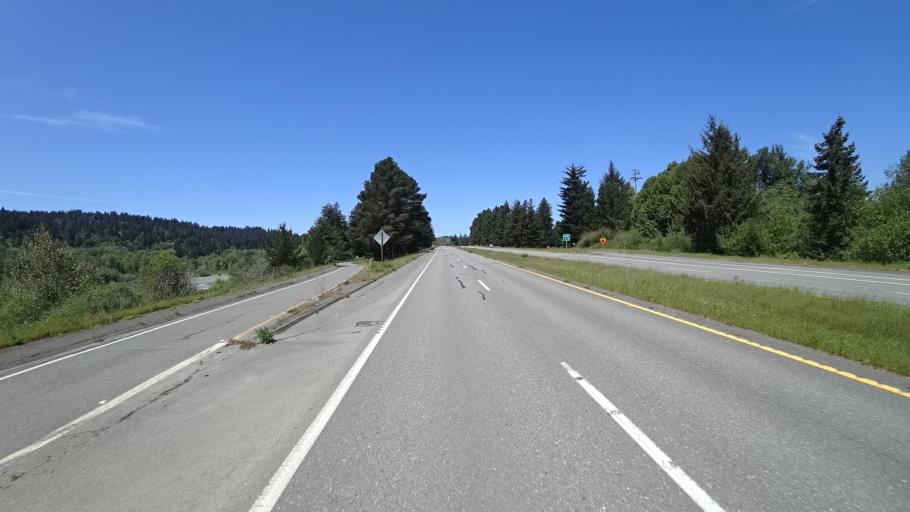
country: US
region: California
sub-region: Humboldt County
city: Blue Lake
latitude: 40.8972
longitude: -124.0192
